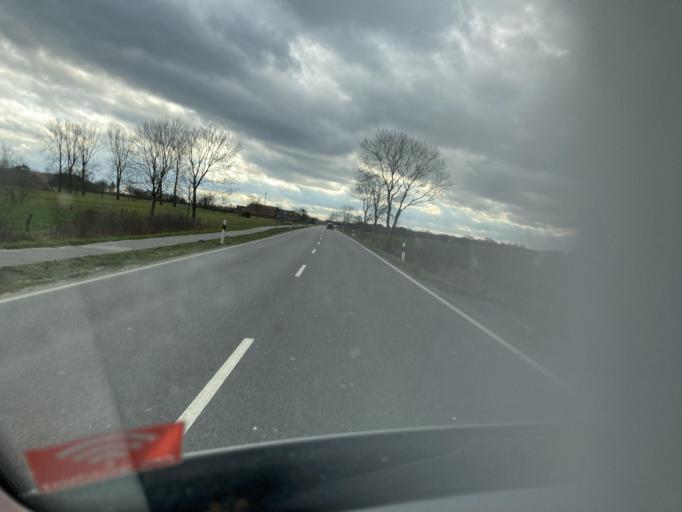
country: DE
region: Lower Saxony
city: Zetel
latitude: 53.4698
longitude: 7.9546
